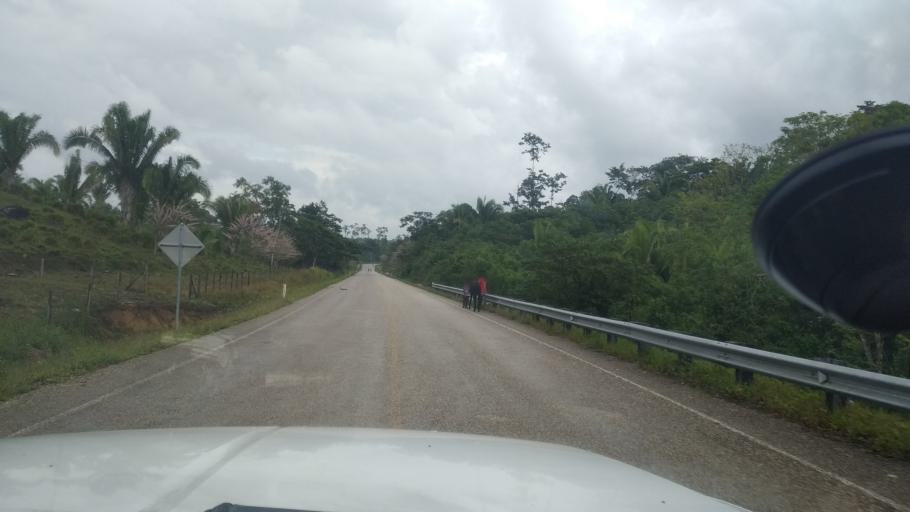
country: GT
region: Peten
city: San Luis
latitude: 16.1992
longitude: -89.1502
